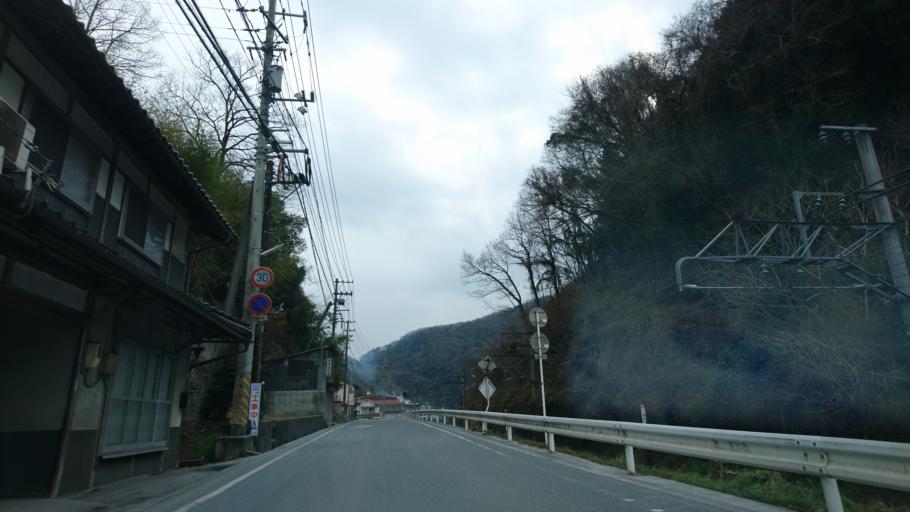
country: JP
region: Okayama
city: Niimi
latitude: 34.9287
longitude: 133.5206
